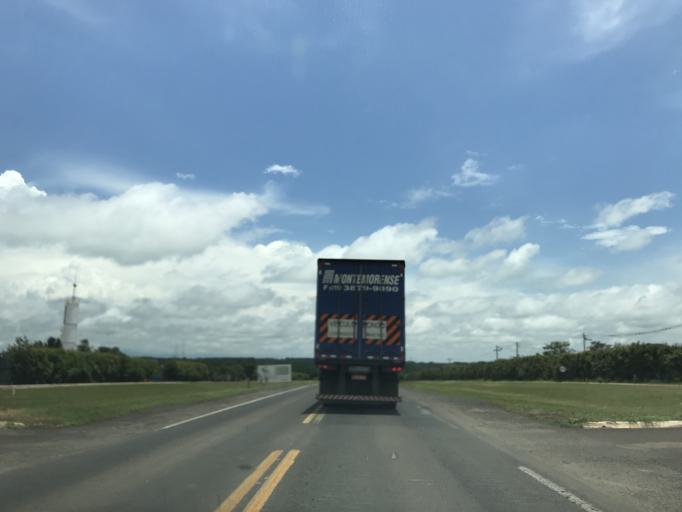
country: BR
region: Minas Gerais
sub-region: Prata
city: Prata
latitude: -19.6511
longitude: -48.9736
